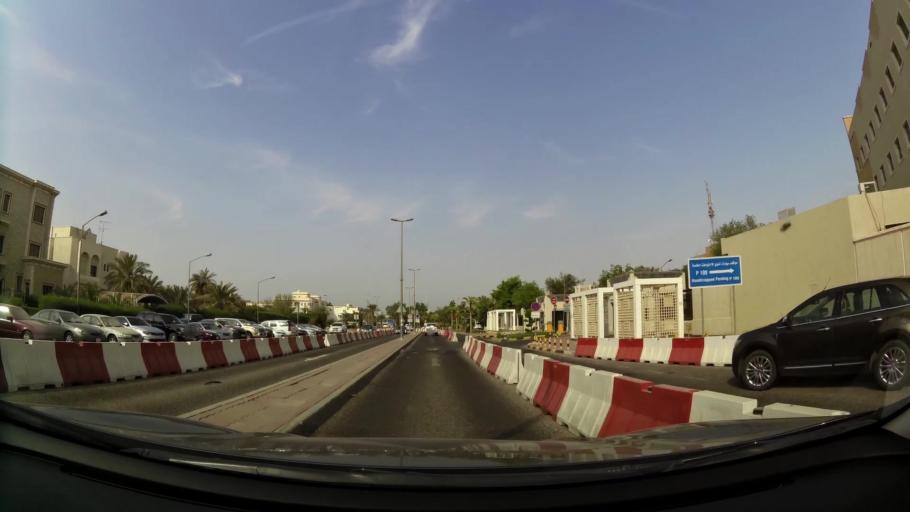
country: KW
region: Al Asimah
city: Ash Shamiyah
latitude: 29.3250
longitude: 47.9702
